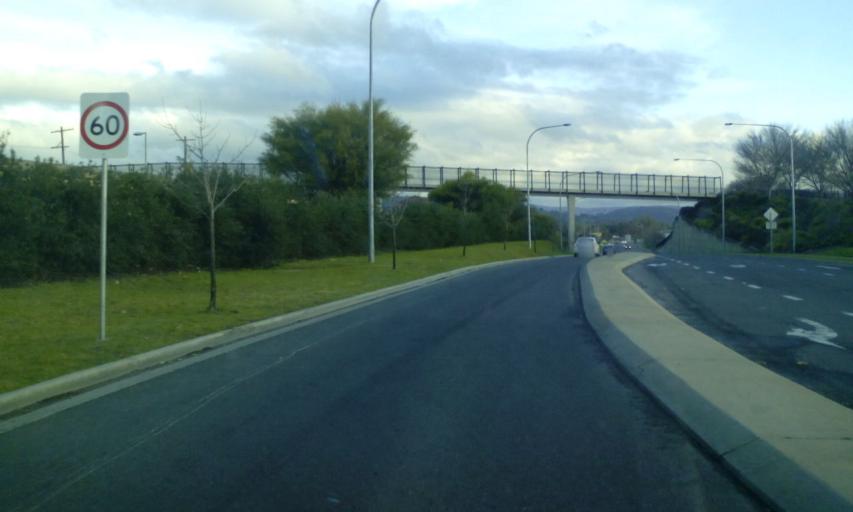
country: AU
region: New South Wales
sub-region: Albury Municipality
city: East Albury
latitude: -36.0862
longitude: 146.9237
